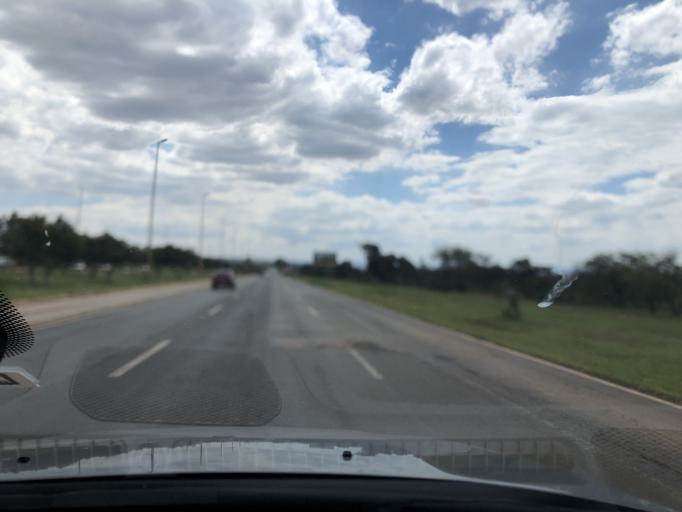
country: BR
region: Federal District
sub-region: Brasilia
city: Brasilia
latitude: -15.9670
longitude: -47.9916
